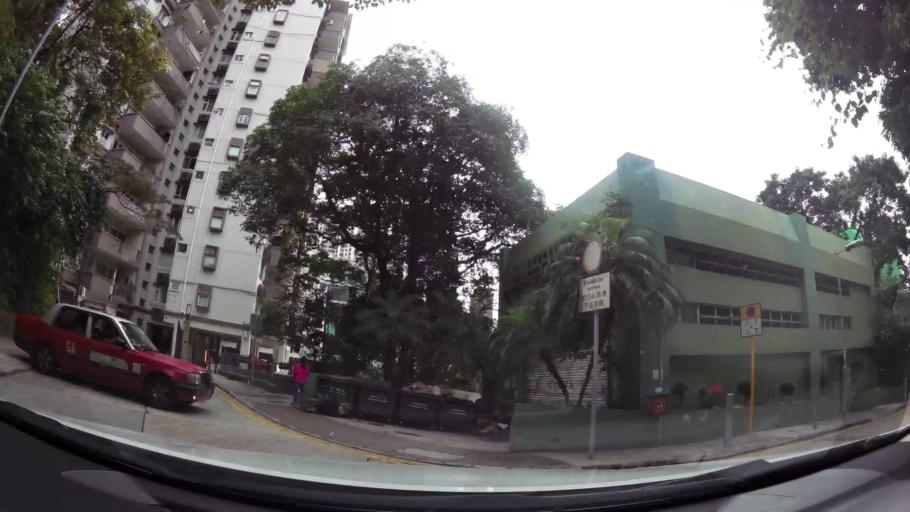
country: HK
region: Wanchai
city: Wan Chai
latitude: 22.2727
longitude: 114.1755
